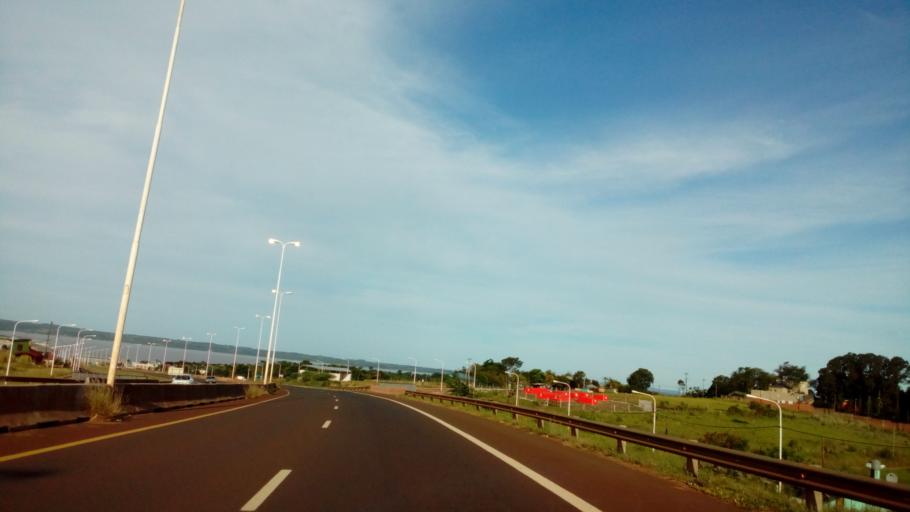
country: AR
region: Misiones
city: Garupa
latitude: -27.4520
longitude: -55.8579
